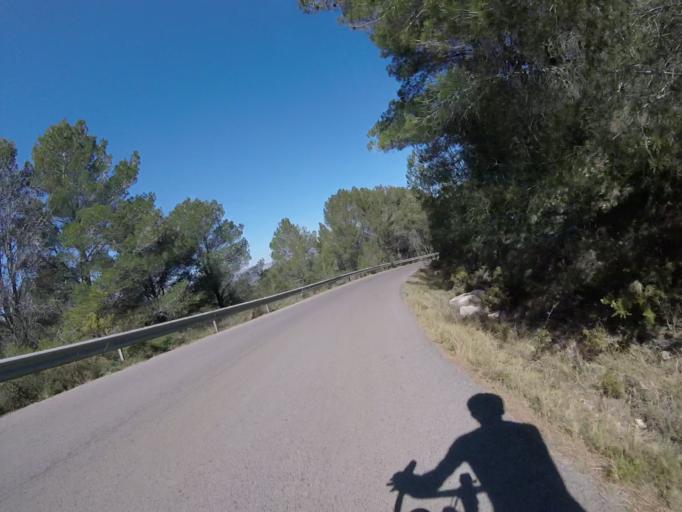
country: ES
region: Valencia
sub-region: Provincia de Castello
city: Cervera del Maestre
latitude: 40.4087
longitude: 0.1949
